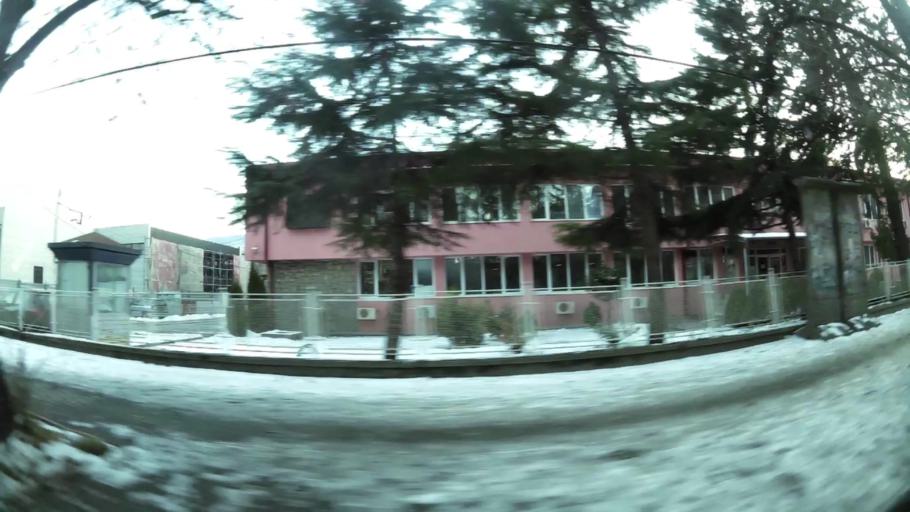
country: MK
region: Karpos
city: Skopje
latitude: 41.9932
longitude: 21.4135
